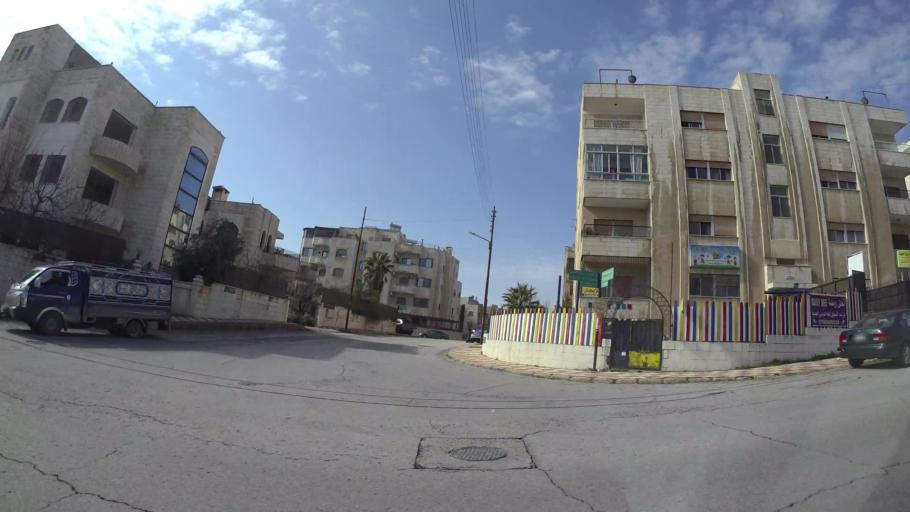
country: JO
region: Amman
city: Al Jubayhah
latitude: 32.0011
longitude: 35.8876
